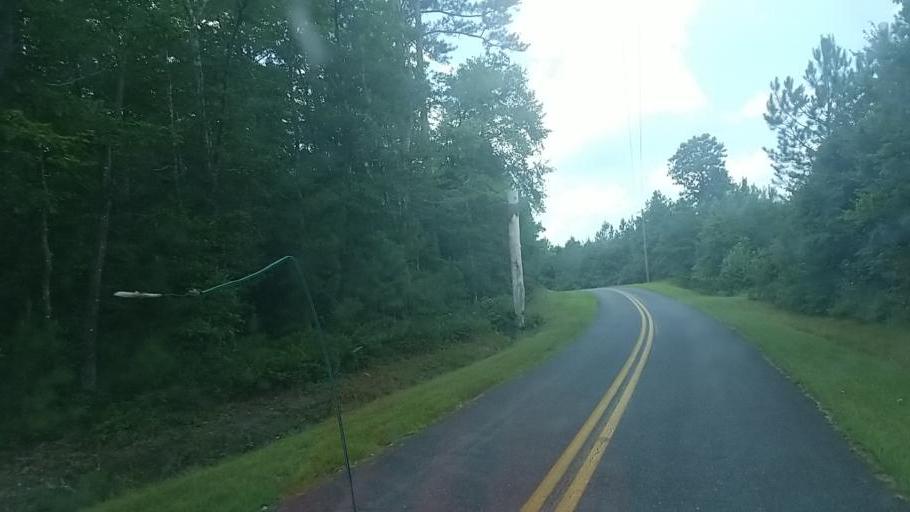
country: US
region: Maryland
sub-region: Worcester County
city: Snow Hill
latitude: 38.2557
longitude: -75.4410
